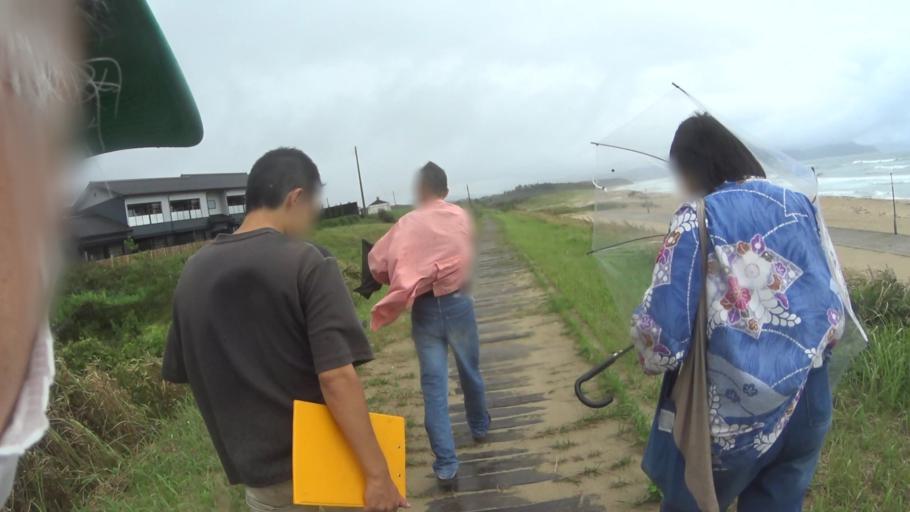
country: JP
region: Hyogo
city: Toyooka
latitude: 35.6625
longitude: 134.9643
